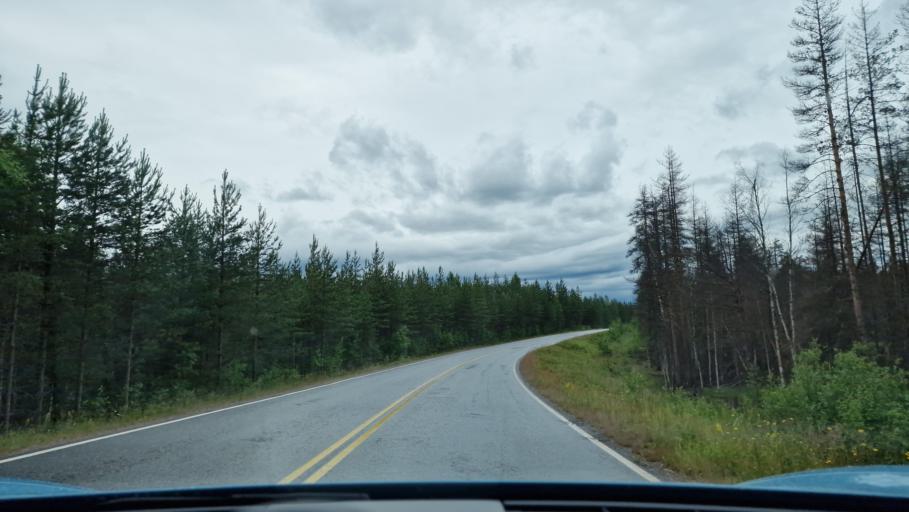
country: FI
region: Central Finland
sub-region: Saarijaervi-Viitasaari
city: Pylkoenmaeki
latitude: 62.6651
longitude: 24.5430
